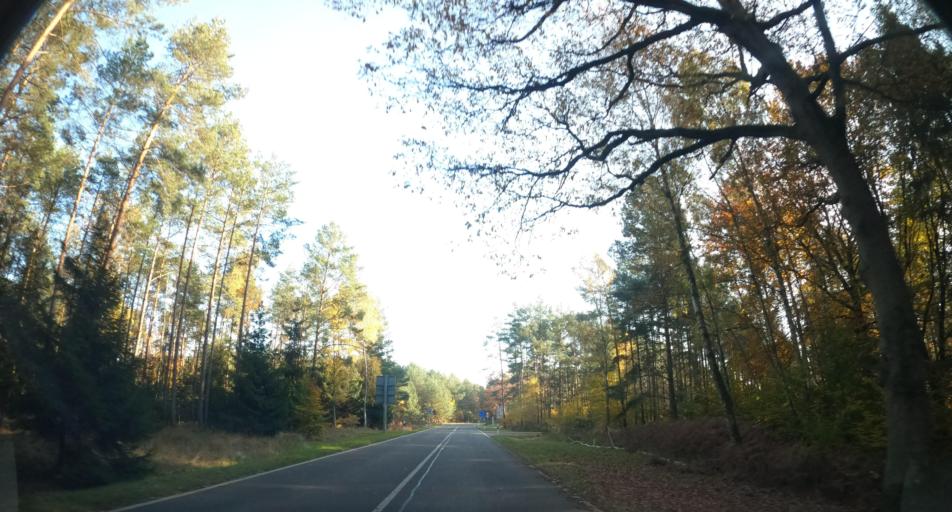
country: PL
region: West Pomeranian Voivodeship
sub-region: Powiat policki
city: Nowe Warpno
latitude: 53.6098
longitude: 14.3150
